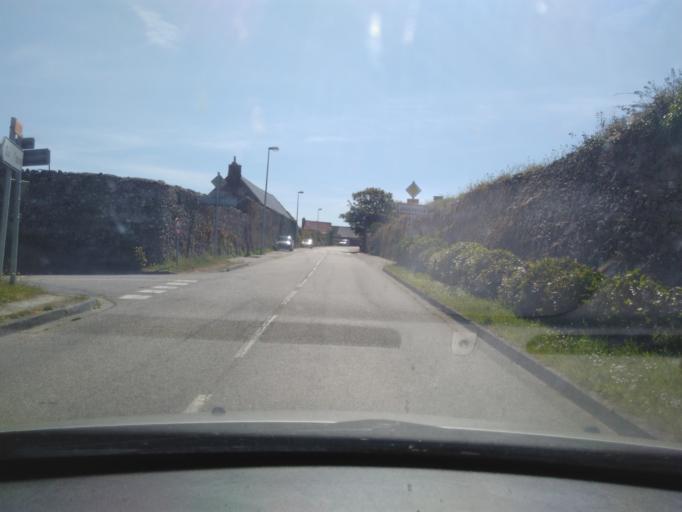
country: FR
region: Lower Normandy
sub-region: Departement de la Manche
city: Beaumont-Hague
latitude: 49.7140
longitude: -1.9325
